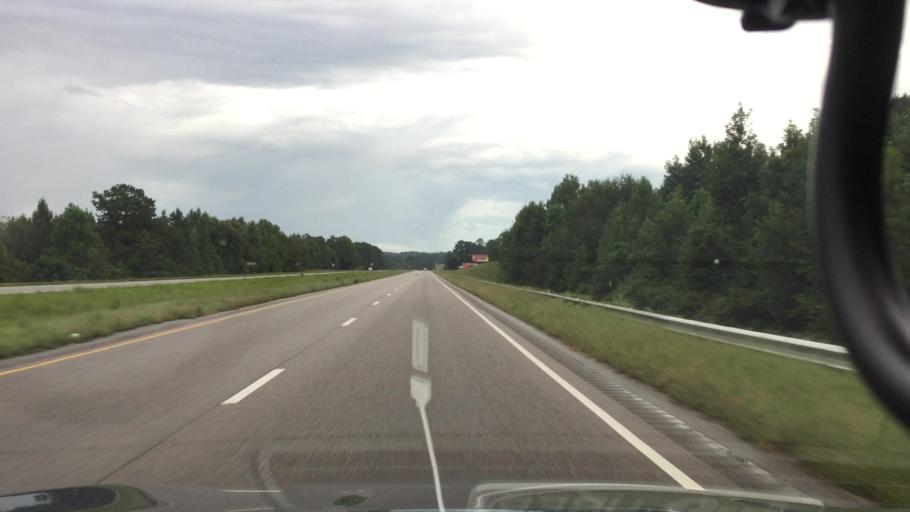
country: US
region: Alabama
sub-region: Pike County
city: Troy
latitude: 31.8618
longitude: -85.9987
